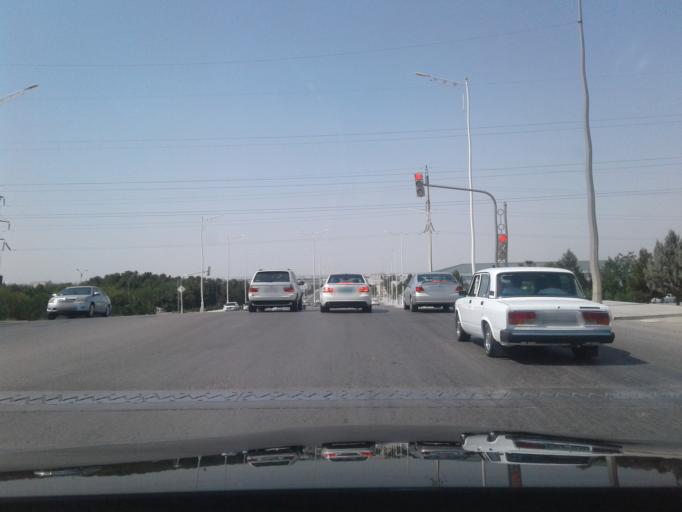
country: TM
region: Ahal
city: Ashgabat
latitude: 37.9050
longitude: 58.4235
